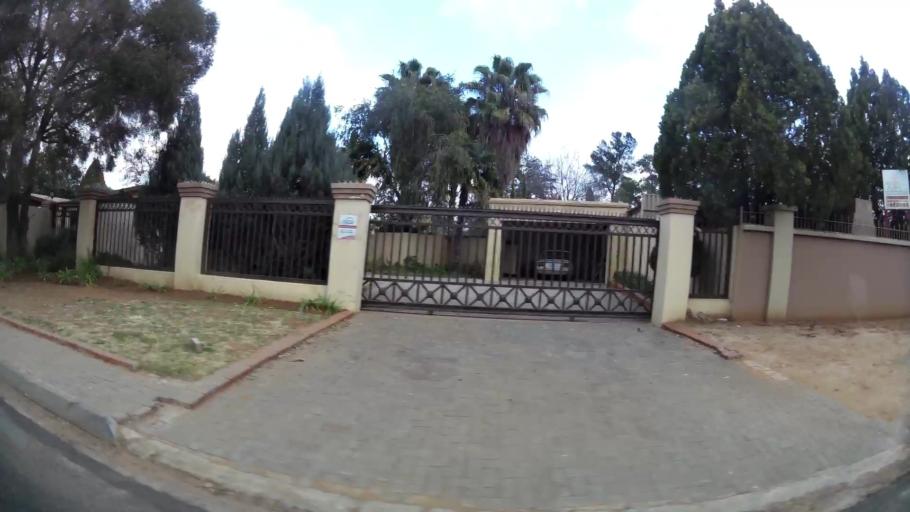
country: ZA
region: Orange Free State
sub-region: Mangaung Metropolitan Municipality
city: Bloemfontein
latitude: -29.1212
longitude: 26.1738
